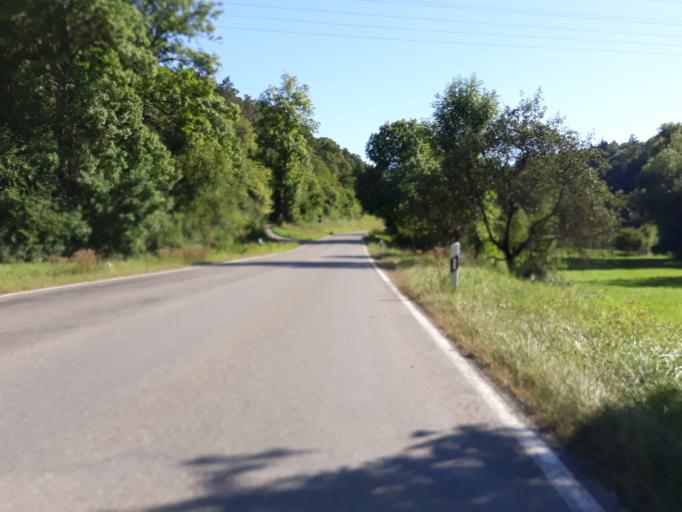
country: DE
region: Baden-Wuerttemberg
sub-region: Regierungsbezirk Stuttgart
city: Aidlingen
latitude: 48.6780
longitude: 8.9119
